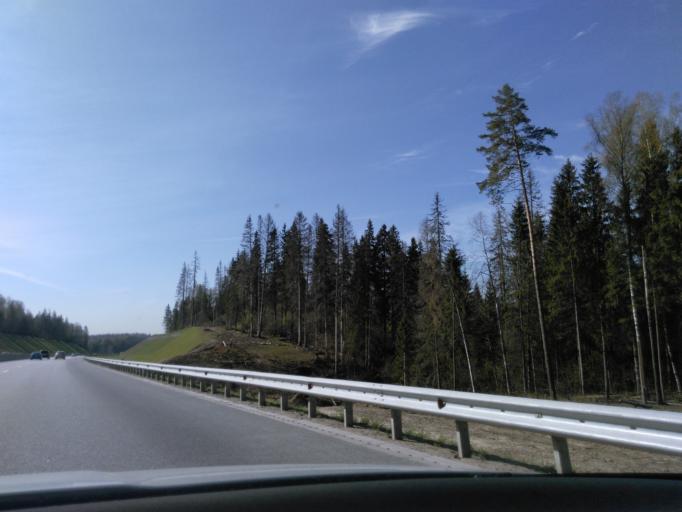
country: RU
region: Moskovskaya
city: Rzhavki
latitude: 56.0451
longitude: 37.2650
